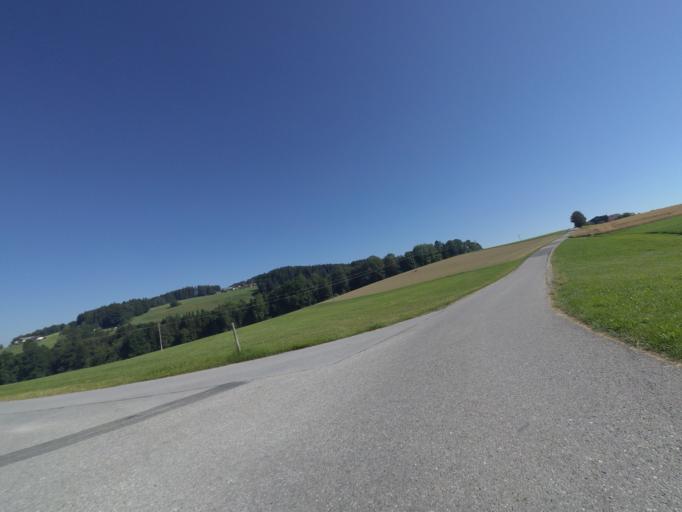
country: AT
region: Salzburg
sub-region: Politischer Bezirk Salzburg-Umgebung
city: Mattsee
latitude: 47.9384
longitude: 13.1106
